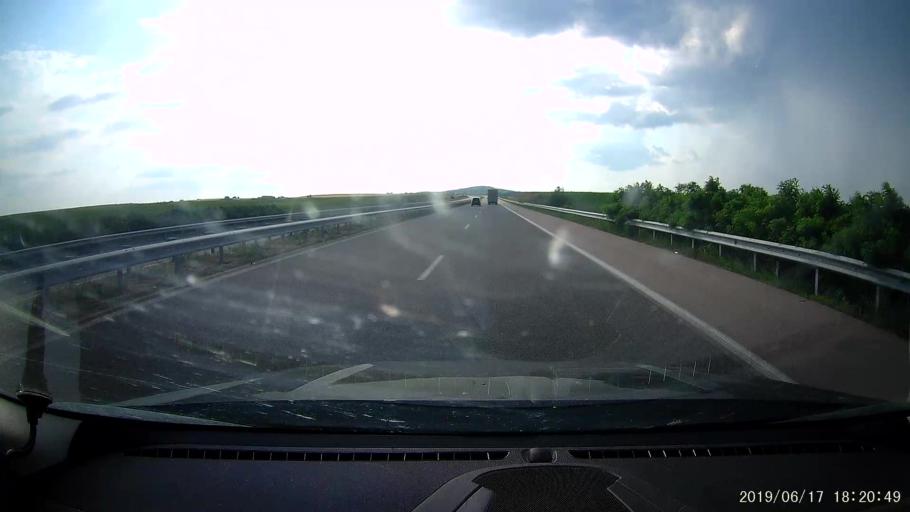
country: BG
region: Khaskovo
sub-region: Obshtina Simeonovgrad
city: Simeonovgrad
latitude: 41.9645
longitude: 25.8015
